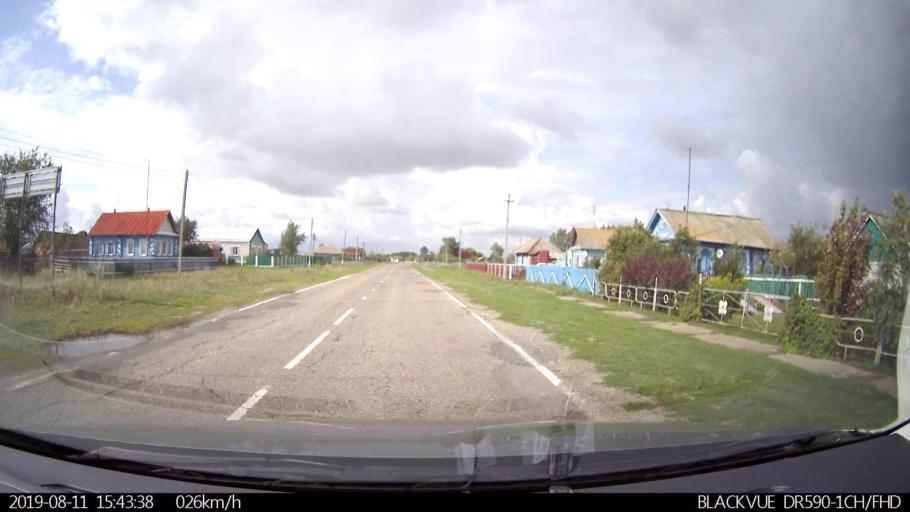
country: RU
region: Ulyanovsk
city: Ignatovka
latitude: 53.8774
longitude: 47.6589
